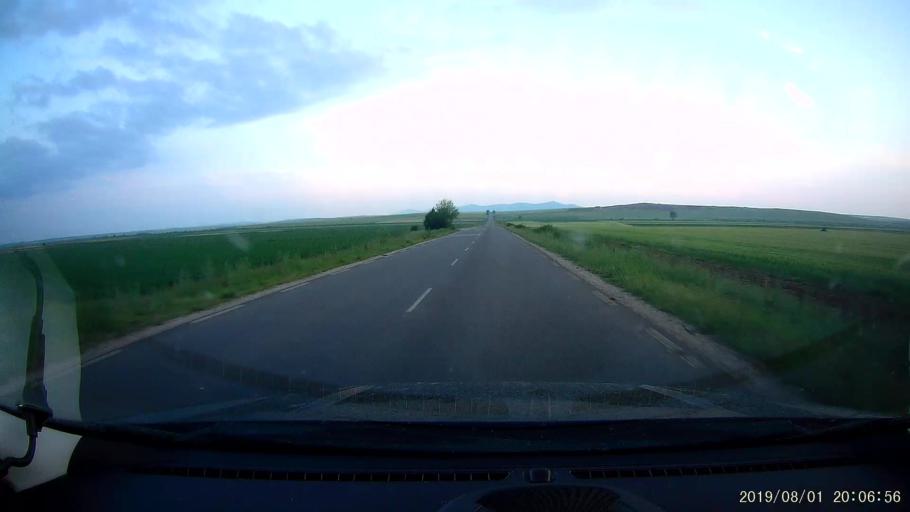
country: BG
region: Yambol
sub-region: Obshtina Yambol
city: Yambol
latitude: 42.5293
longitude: 26.5598
